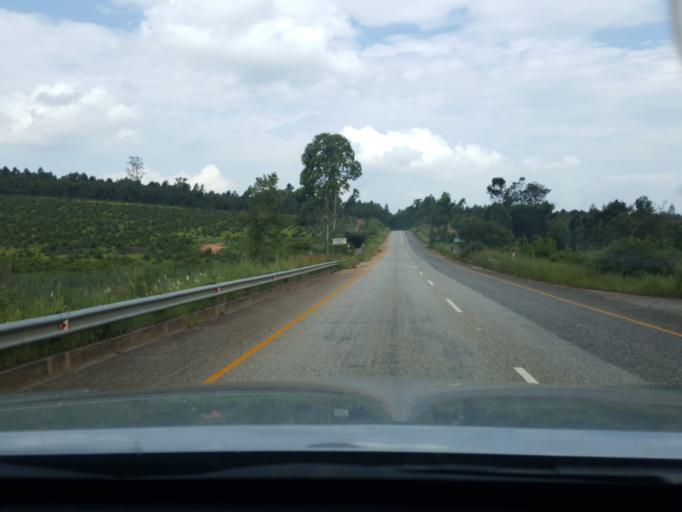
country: ZA
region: Mpumalanga
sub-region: Ehlanzeni District
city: White River
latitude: -25.1799
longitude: 30.8792
